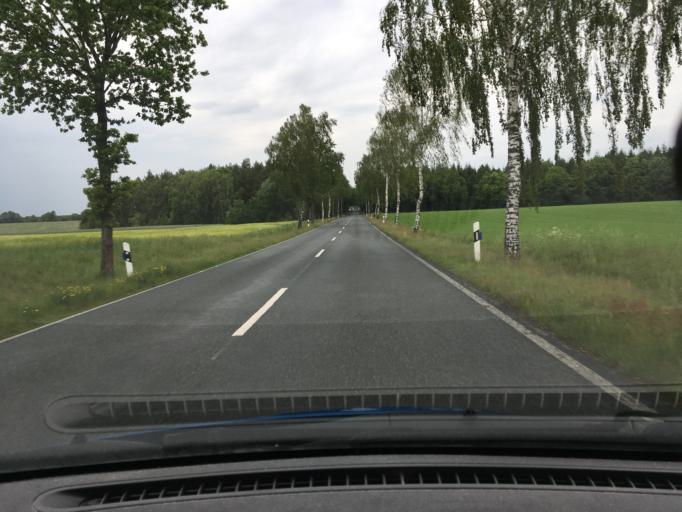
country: DE
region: Lower Saxony
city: Egestorf
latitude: 53.1298
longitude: 10.0473
